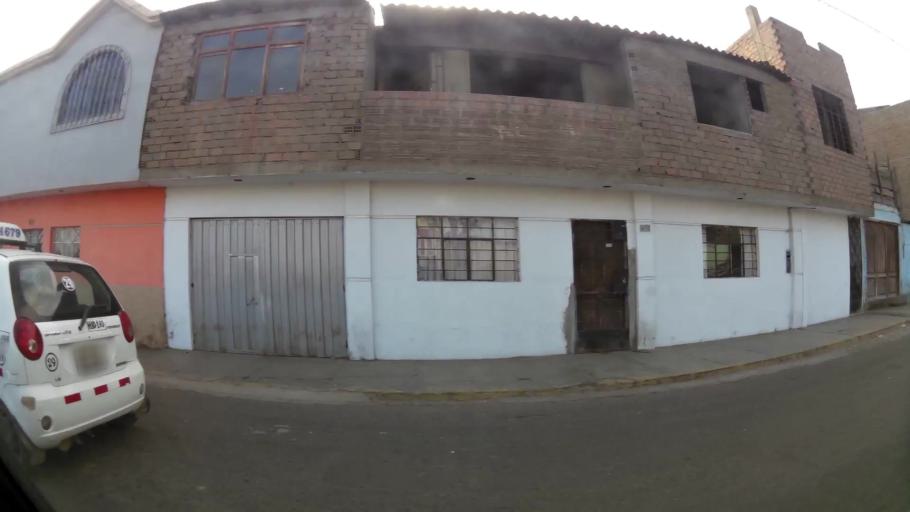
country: PE
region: La Libertad
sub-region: Provincia de Trujillo
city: El Porvenir
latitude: -8.0934
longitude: -79.0149
